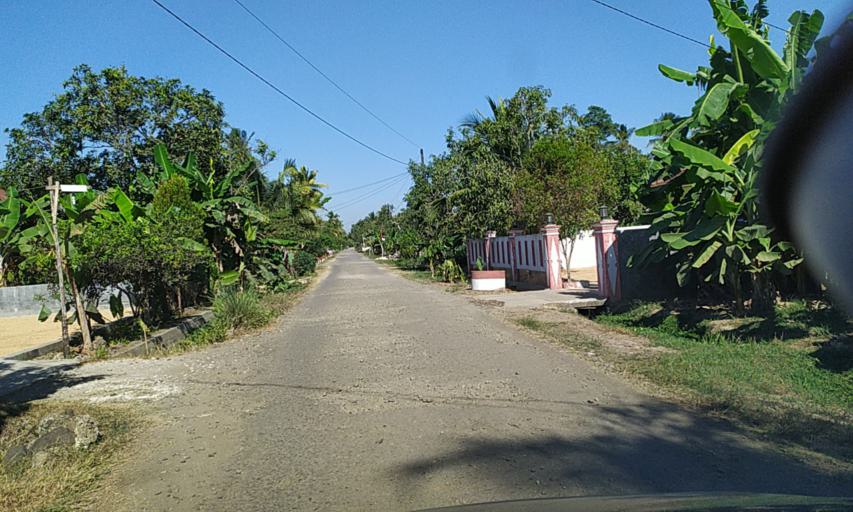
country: ID
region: Central Java
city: Kalenaren
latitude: -7.5811
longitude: 108.7881
